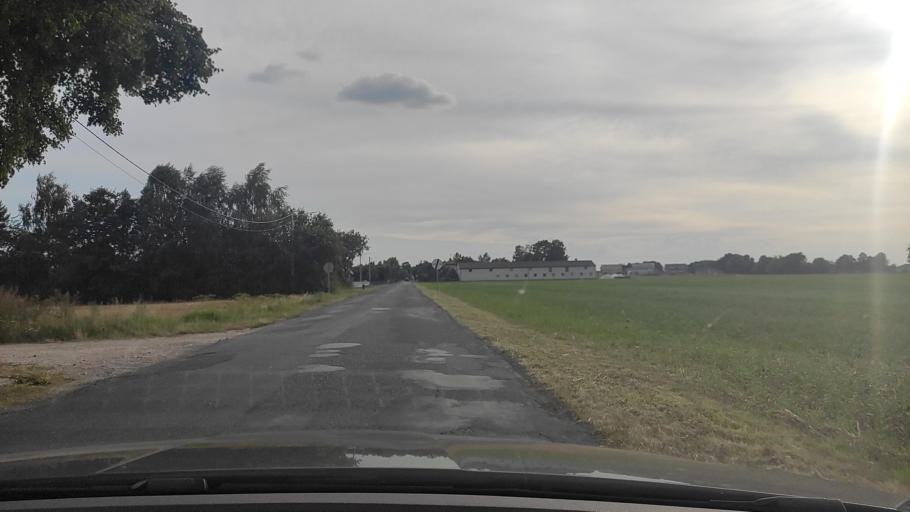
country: PL
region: Greater Poland Voivodeship
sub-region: Powiat poznanski
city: Kleszczewo
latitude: 52.3740
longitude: 17.1577
